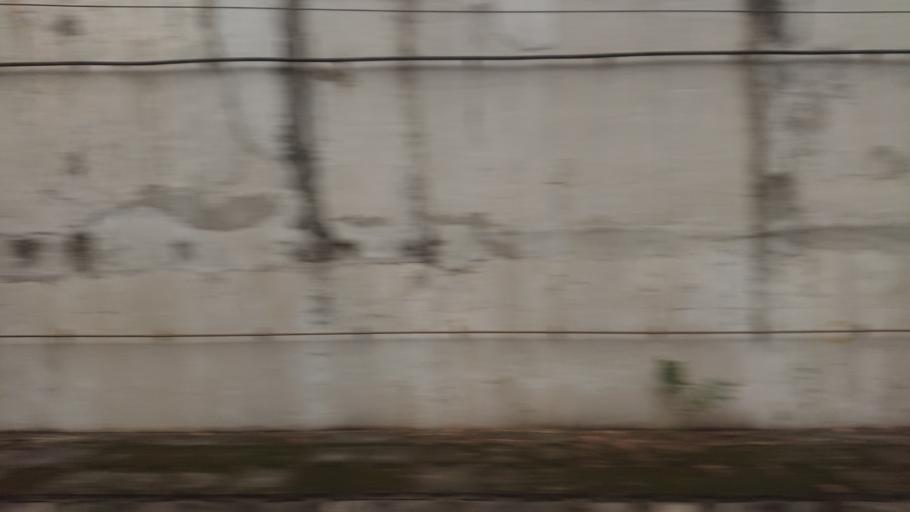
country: TW
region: Taiwan
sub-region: Hualien
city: Hualian
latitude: 23.8200
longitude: 121.4763
